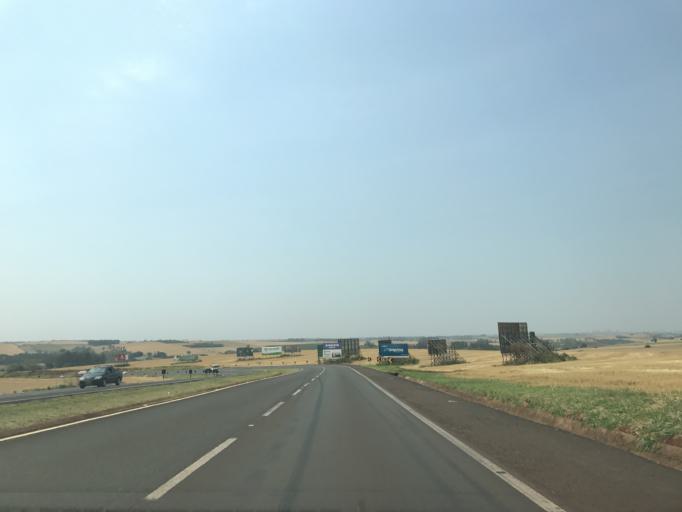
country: BR
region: Parana
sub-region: Rolandia
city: Rolandia
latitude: -23.3397
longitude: -51.3522
